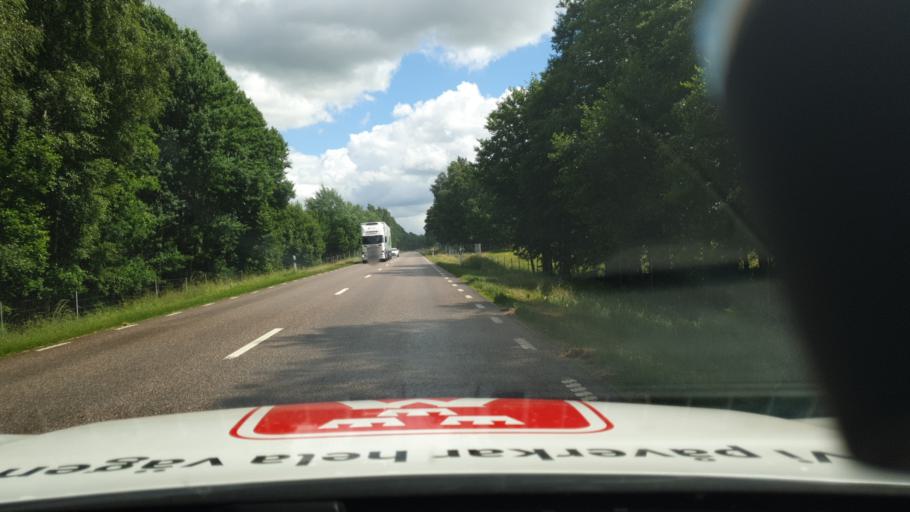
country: SE
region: Vaestra Goetaland
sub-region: Falkopings Kommun
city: Floby
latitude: 58.1916
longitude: 13.3414
